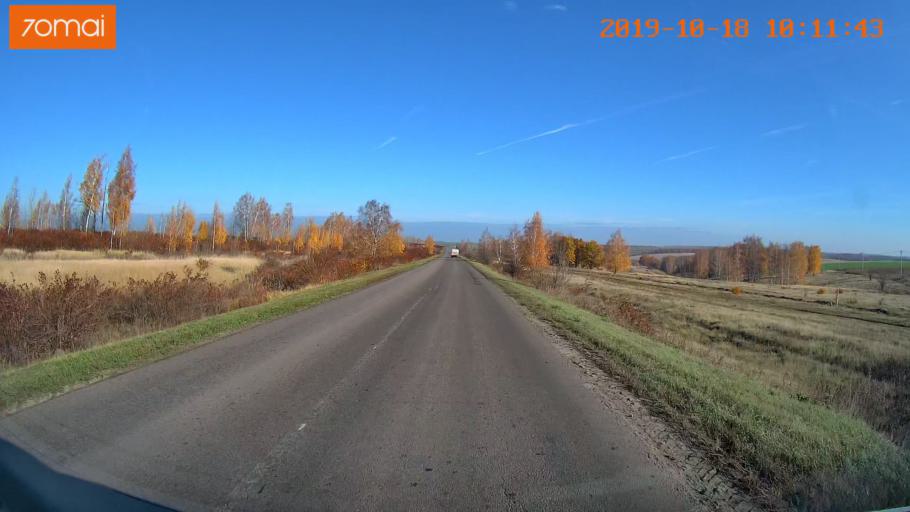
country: RU
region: Tula
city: Kurkino
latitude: 53.3853
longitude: 38.5020
